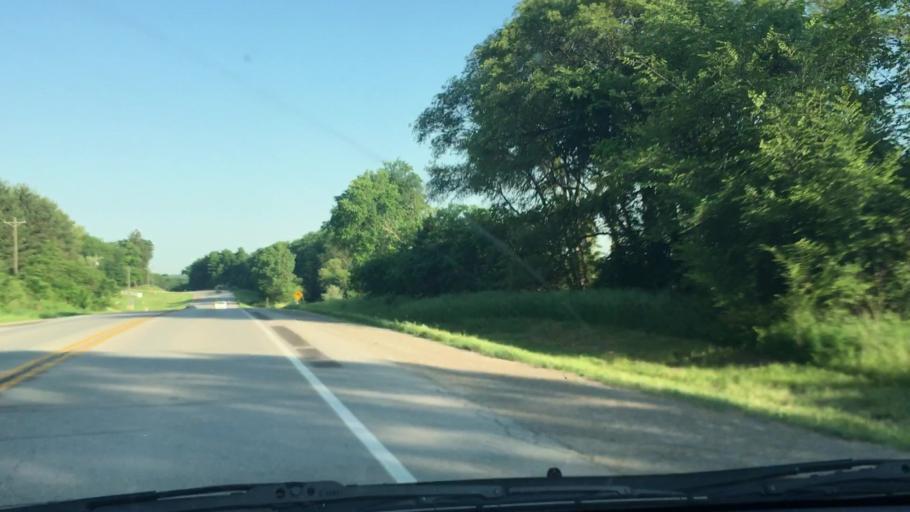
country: US
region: Iowa
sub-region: Johnson County
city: Tiffin
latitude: 41.7097
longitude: -91.6886
